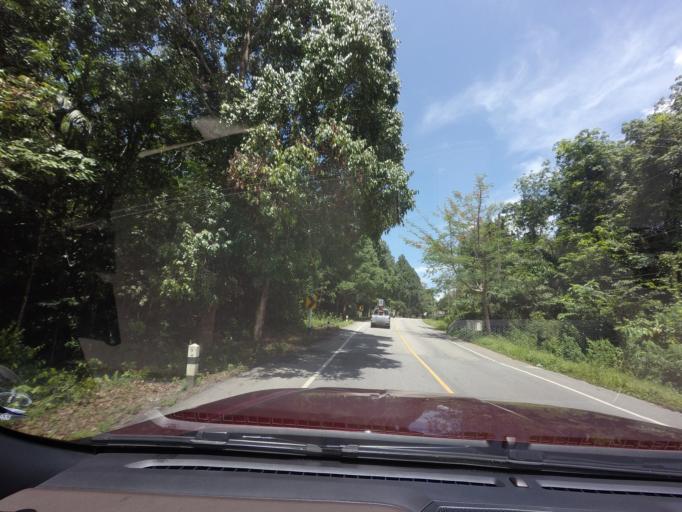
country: TH
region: Narathiwat
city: Chanae
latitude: 6.1384
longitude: 101.7012
